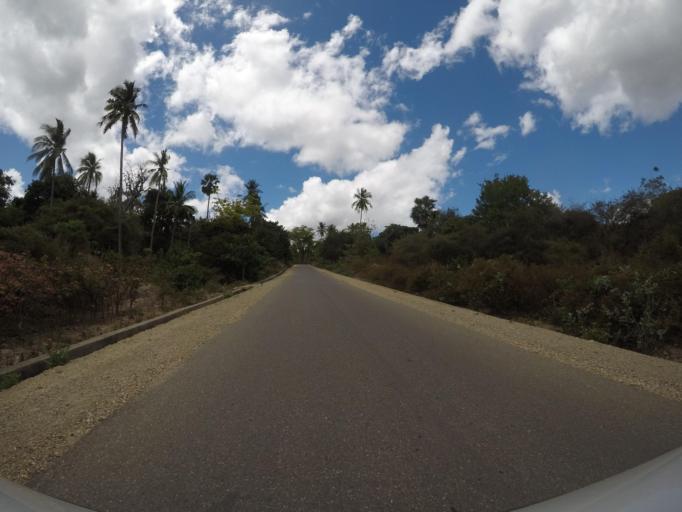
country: TL
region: Lautem
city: Lospalos
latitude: -8.3544
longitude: 126.9293
